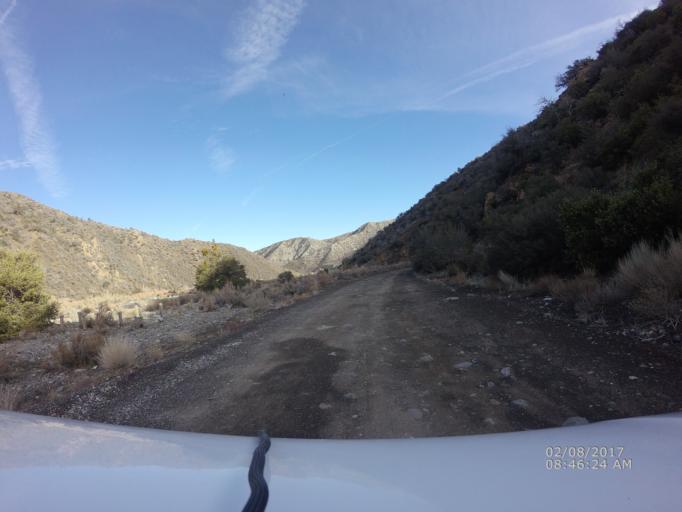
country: US
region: California
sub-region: San Bernardino County
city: Pinon Hills
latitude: 34.4026
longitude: -117.8242
